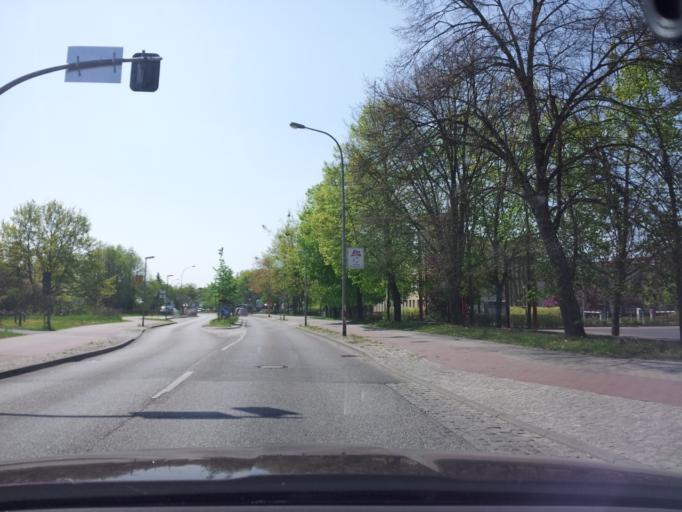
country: DE
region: Brandenburg
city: Kleinmachnow
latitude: 52.3958
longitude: 13.2408
